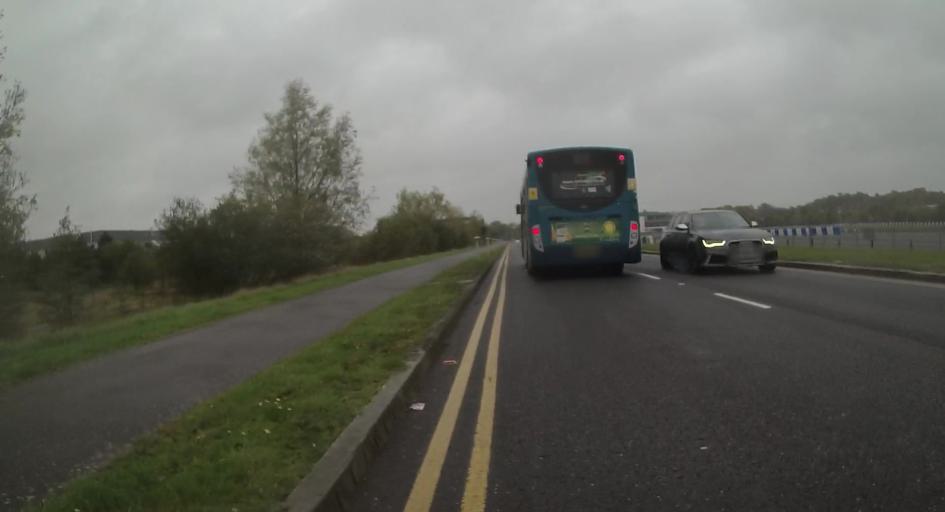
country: GB
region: England
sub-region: Surrey
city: Byfleet
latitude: 51.3489
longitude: -0.4707
